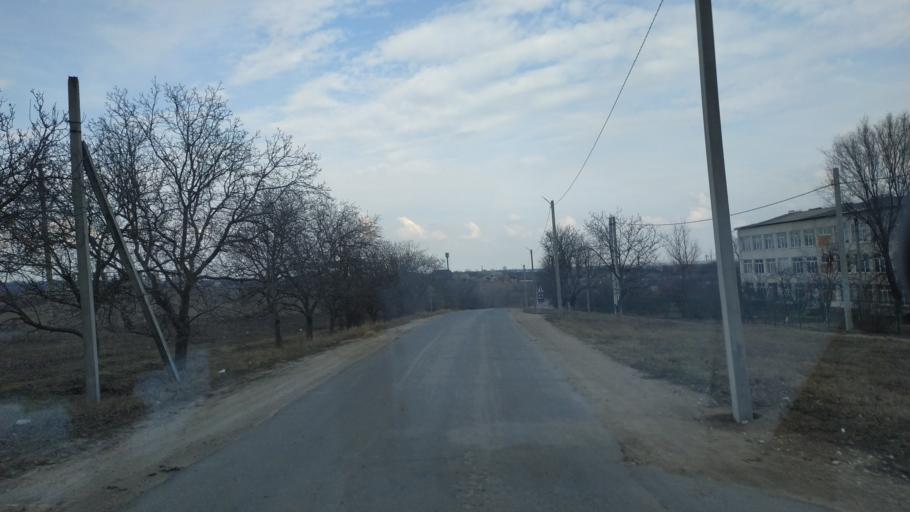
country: MD
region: Anenii Noi
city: Anenii Noi
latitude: 46.9006
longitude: 29.3121
